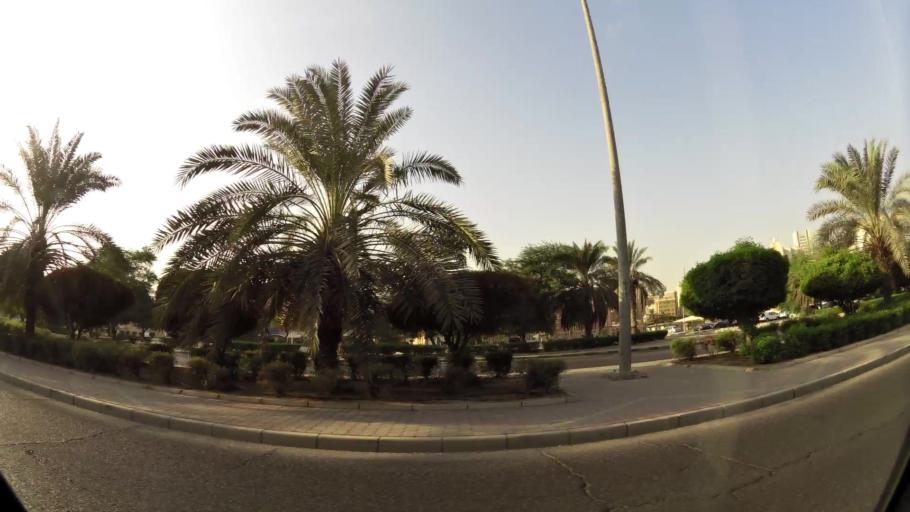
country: KW
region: Muhafazat Hawalli
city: Hawalli
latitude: 29.3467
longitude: 48.0230
